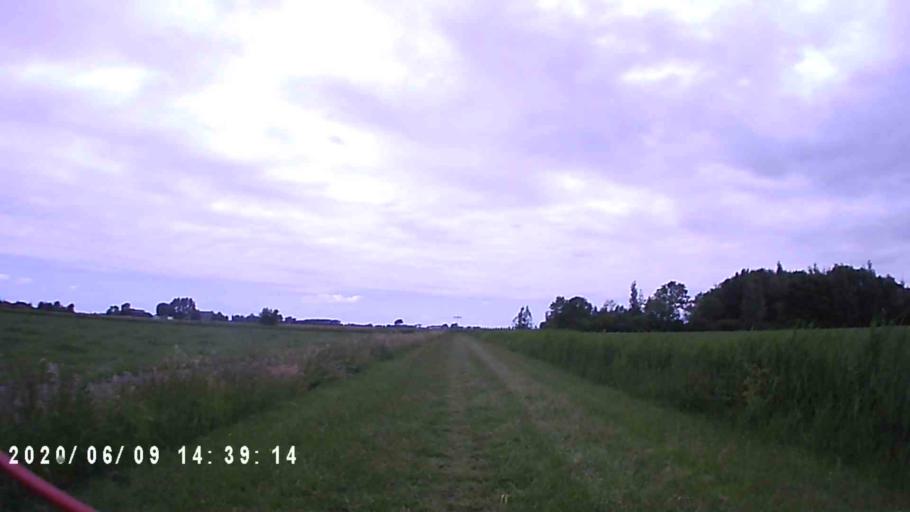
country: NL
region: Groningen
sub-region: Gemeente Bedum
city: Bedum
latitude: 53.3301
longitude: 6.5775
